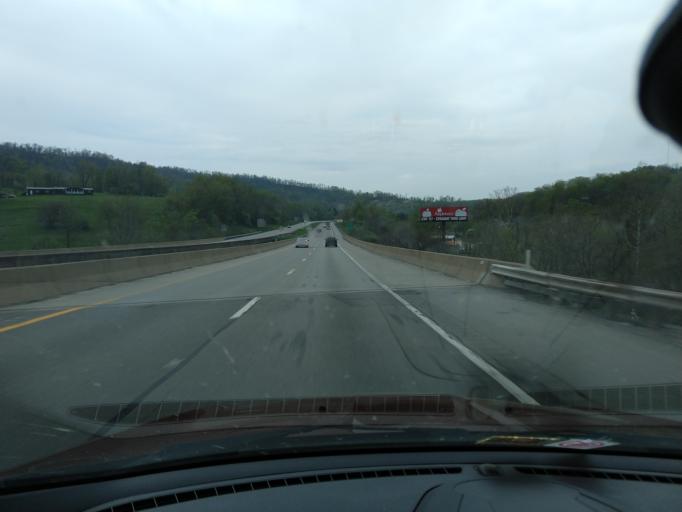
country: US
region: West Virginia
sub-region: Lewis County
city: Weston
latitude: 39.1218
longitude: -80.3868
